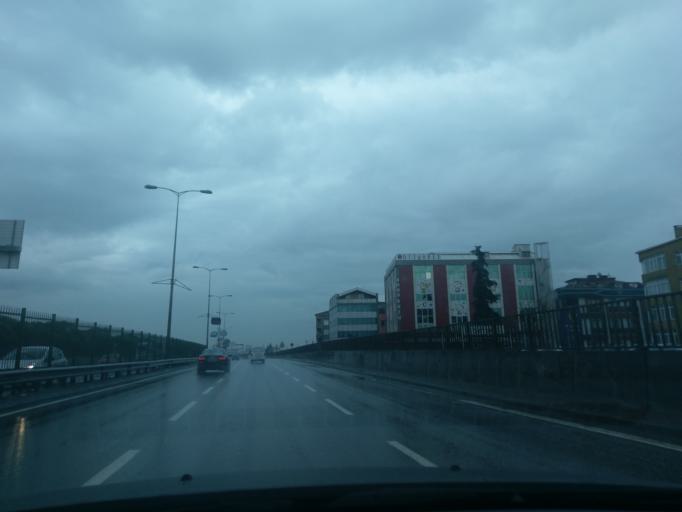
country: TR
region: Istanbul
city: Samandira
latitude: 41.0138
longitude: 29.1976
